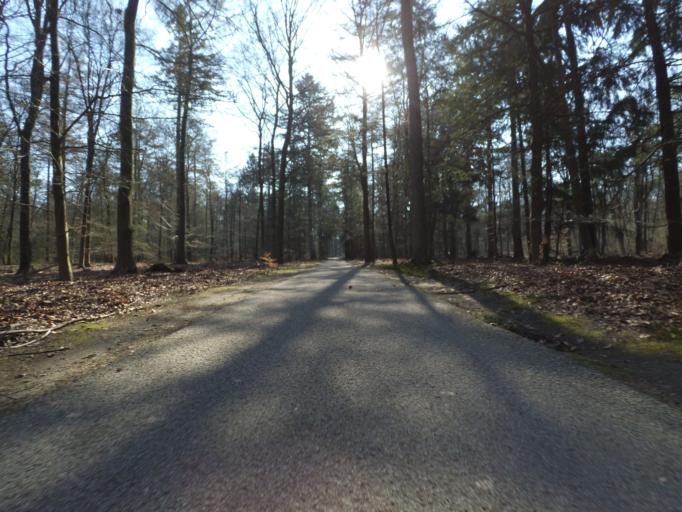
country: NL
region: Gelderland
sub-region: Gemeente Ede
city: Otterlo
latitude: 52.1028
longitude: 5.7896
